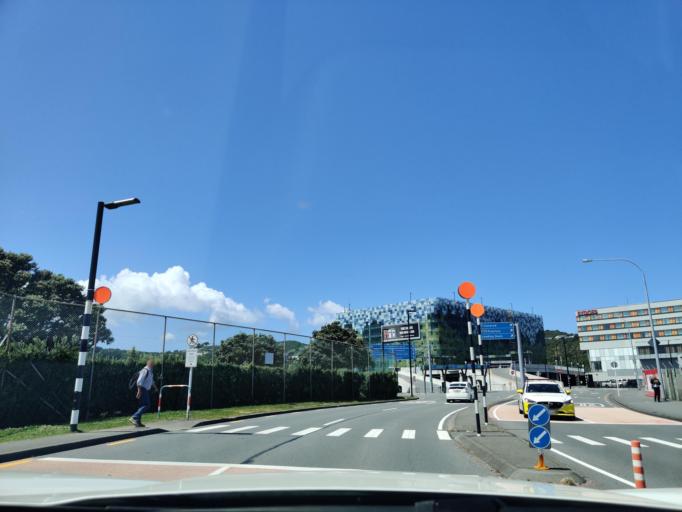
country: NZ
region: Wellington
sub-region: Wellington City
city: Wellington
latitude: -41.3265
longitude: 174.8113
